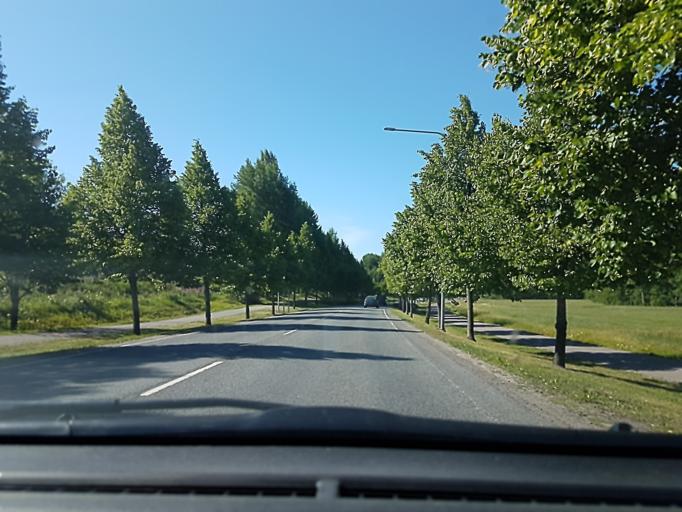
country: FI
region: Uusimaa
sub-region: Helsinki
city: Vantaa
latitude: 60.3445
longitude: 25.0741
